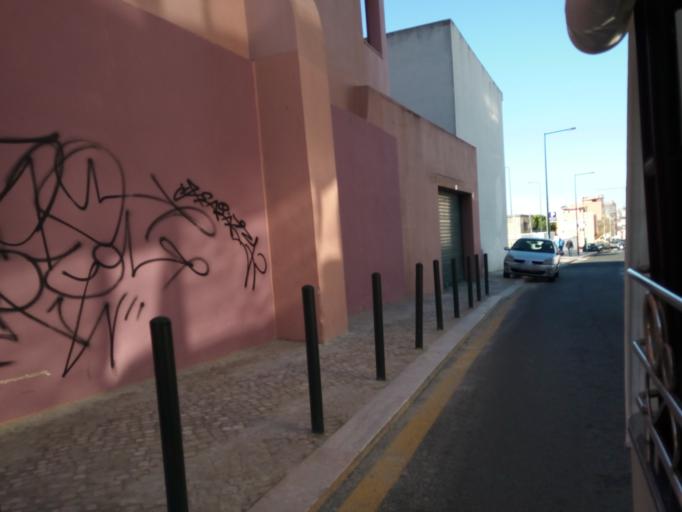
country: PT
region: Lisbon
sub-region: Lisbon
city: Lisbon
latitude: 38.7181
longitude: -9.1301
